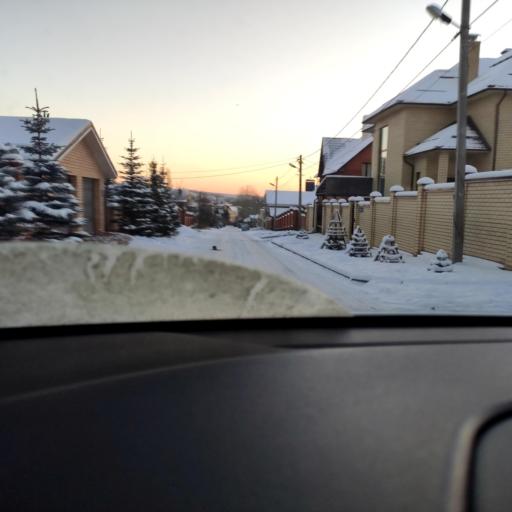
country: RU
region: Tatarstan
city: Stolbishchi
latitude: 55.7482
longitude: 49.2486
